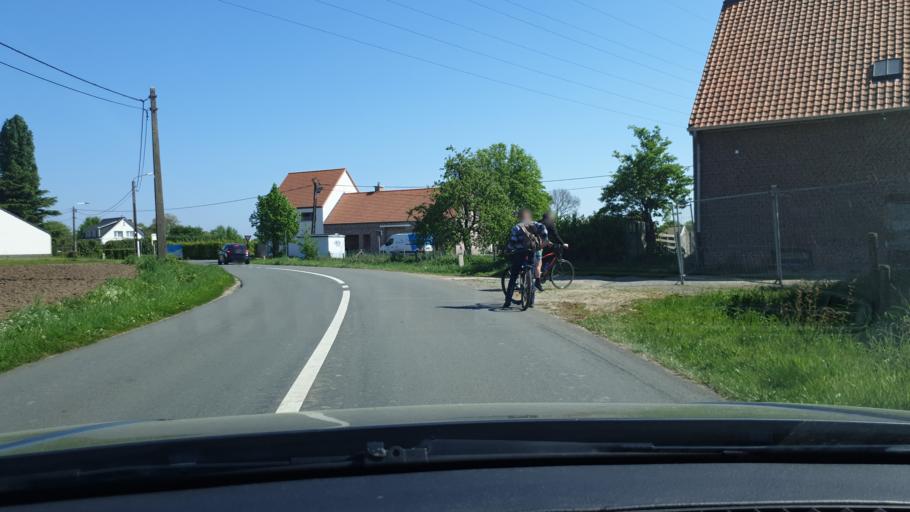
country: BE
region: Flanders
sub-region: Provincie Antwerpen
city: Geel
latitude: 51.1550
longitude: 4.9538
